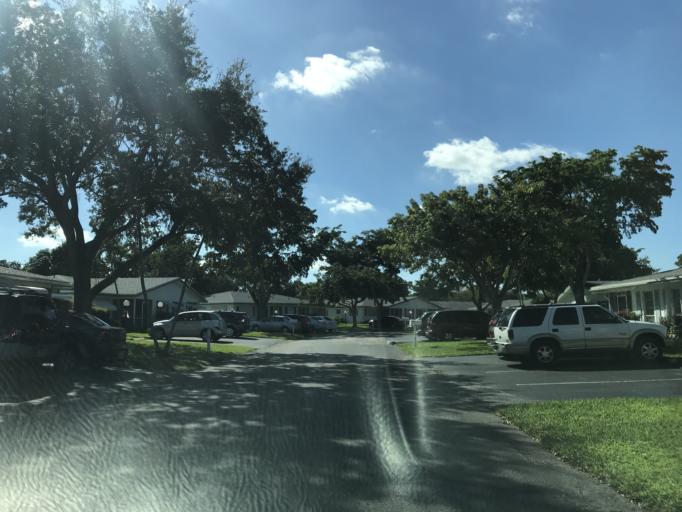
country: US
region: Florida
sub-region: Broward County
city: Plantation
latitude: 26.1373
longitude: -80.2616
